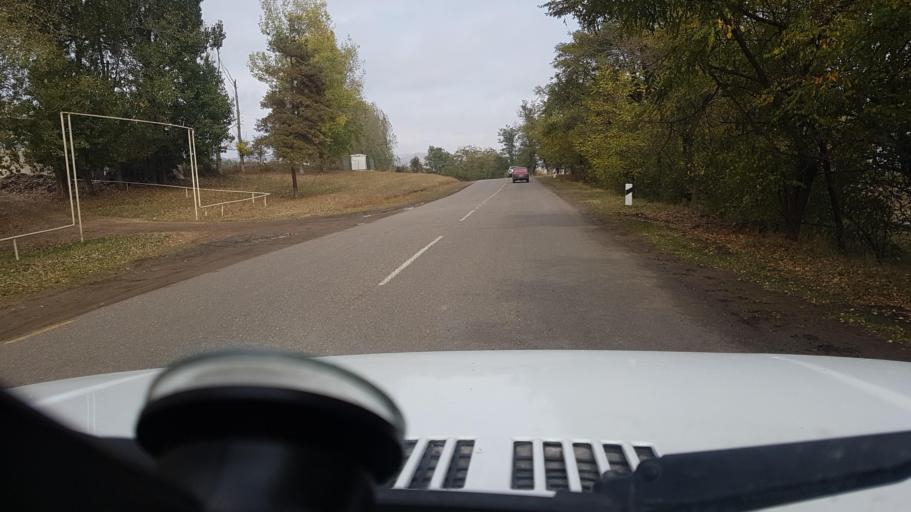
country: AZ
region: Gadabay Rayon
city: Ariqdam
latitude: 40.6443
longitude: 45.8128
